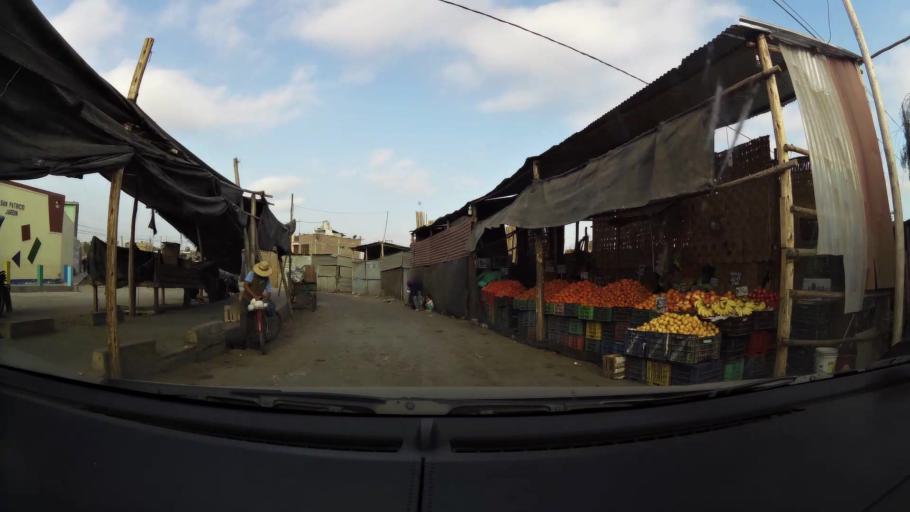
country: PE
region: La Libertad
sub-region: Provincia de Trujillo
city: La Esperanza
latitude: -8.0892
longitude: -79.0235
